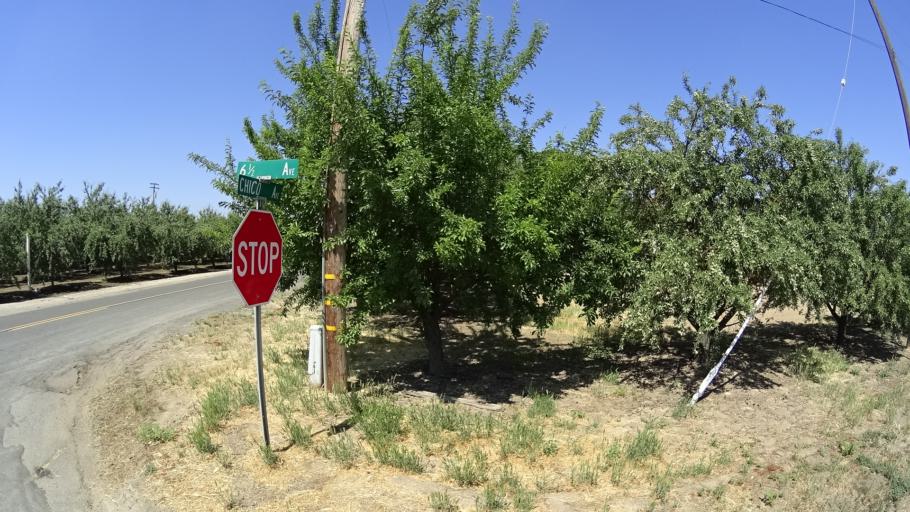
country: US
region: California
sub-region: Fresno County
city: Kingsburg
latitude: 36.4597
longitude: -119.5734
